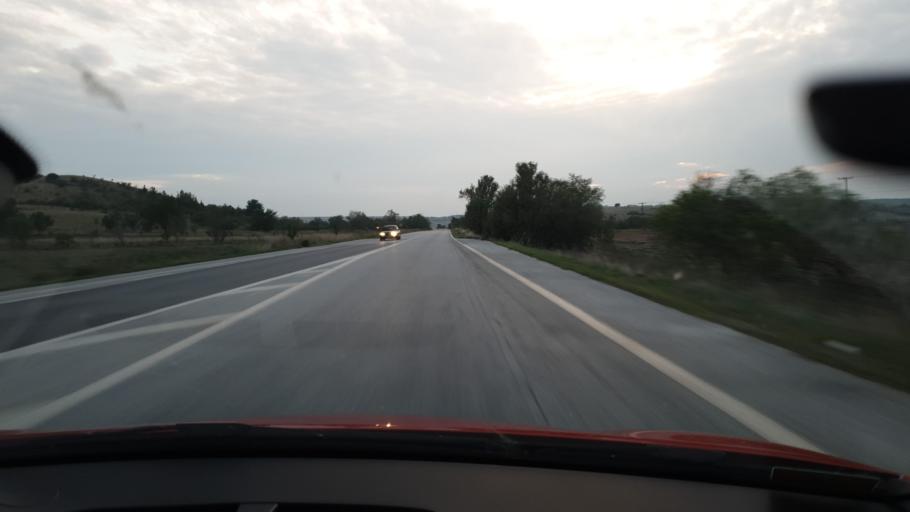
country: GR
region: Central Macedonia
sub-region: Nomos Kilkis
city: Kristoni
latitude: 40.9984
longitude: 22.7664
